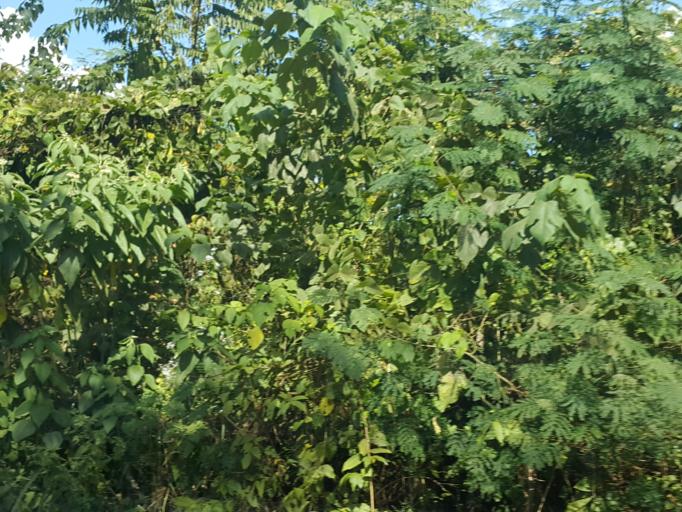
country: TH
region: Chiang Mai
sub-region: Amphoe Chiang Dao
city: Chiang Dao
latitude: 19.3993
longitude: 98.9296
